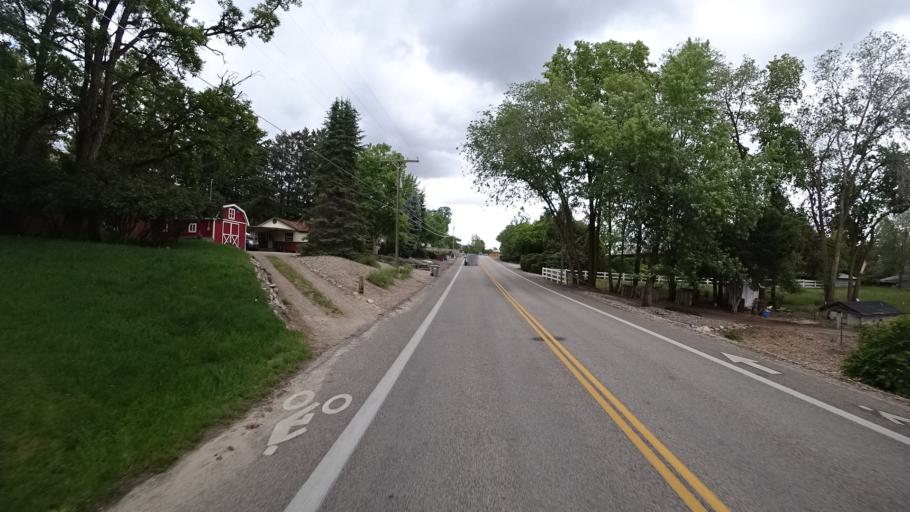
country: US
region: Idaho
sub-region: Ada County
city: Garden City
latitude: 43.6756
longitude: -116.2629
